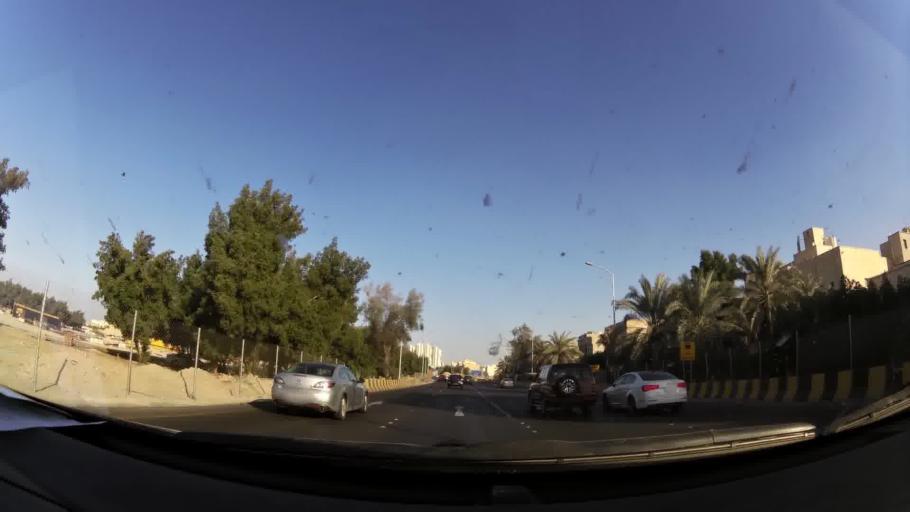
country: KW
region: Mubarak al Kabir
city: Sabah as Salim
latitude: 29.2639
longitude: 48.0634
